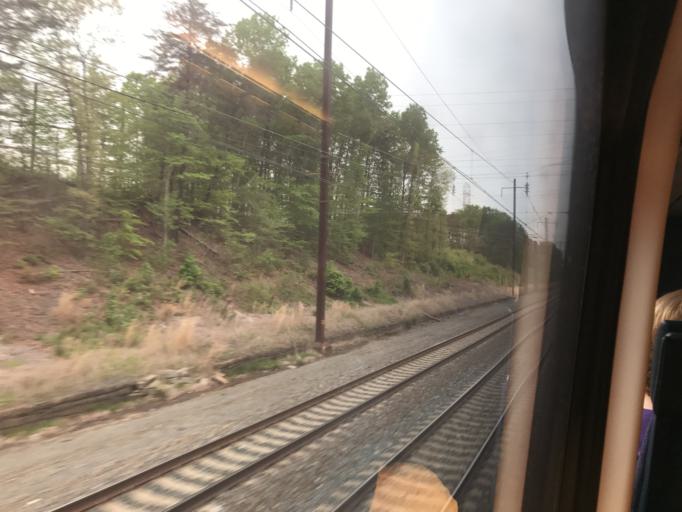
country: US
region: Maryland
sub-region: Prince George's County
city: Glenn Dale
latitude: 39.0126
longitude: -76.7710
